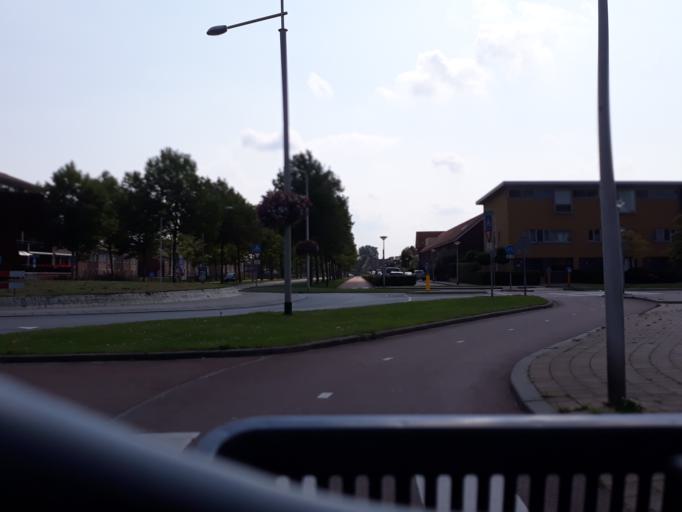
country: NL
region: South Holland
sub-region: Gemeente Hendrik-Ido-Ambacht
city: Hendrik-Ido-Ambacht
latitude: 51.8336
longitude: 4.6493
